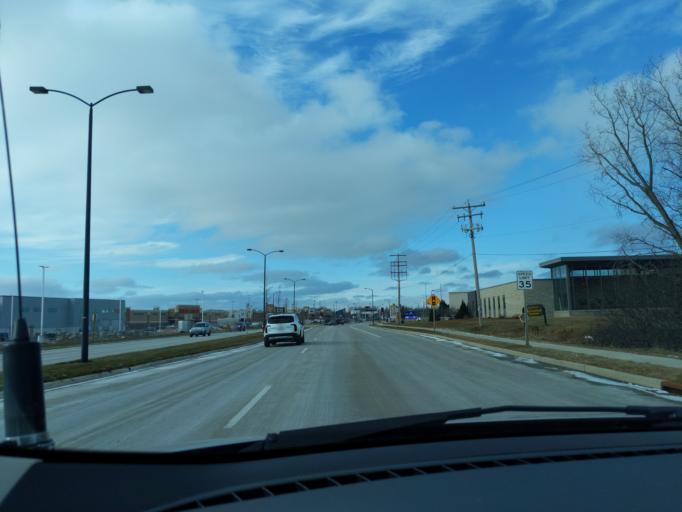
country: US
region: Wisconsin
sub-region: Brown County
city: Ashwaubenon
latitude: 44.4810
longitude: -88.0633
